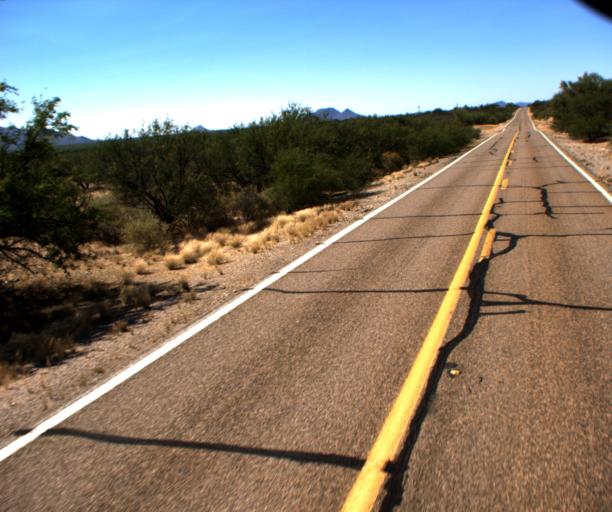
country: US
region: Arizona
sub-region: Pima County
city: Three Points
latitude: 31.9219
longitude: -111.3906
